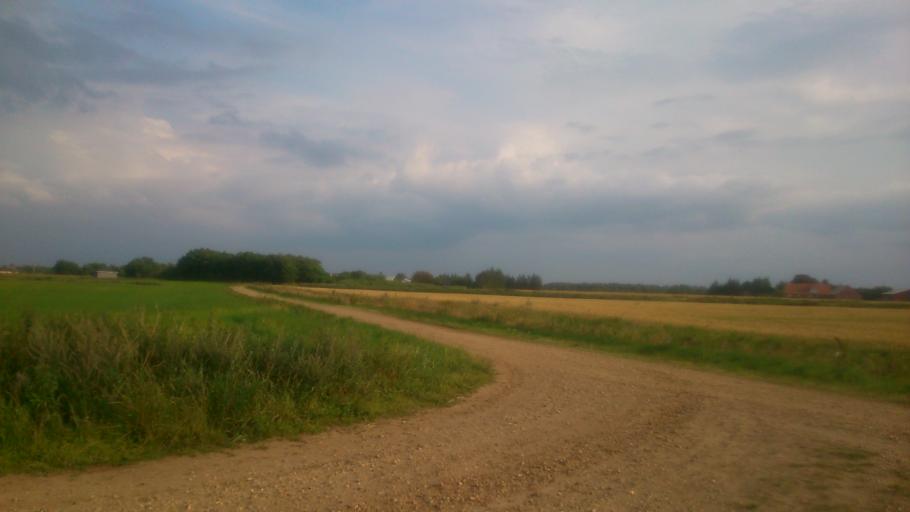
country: DK
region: Central Jutland
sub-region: Ringkobing-Skjern Kommune
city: Tarm
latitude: 55.9147
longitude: 8.4982
